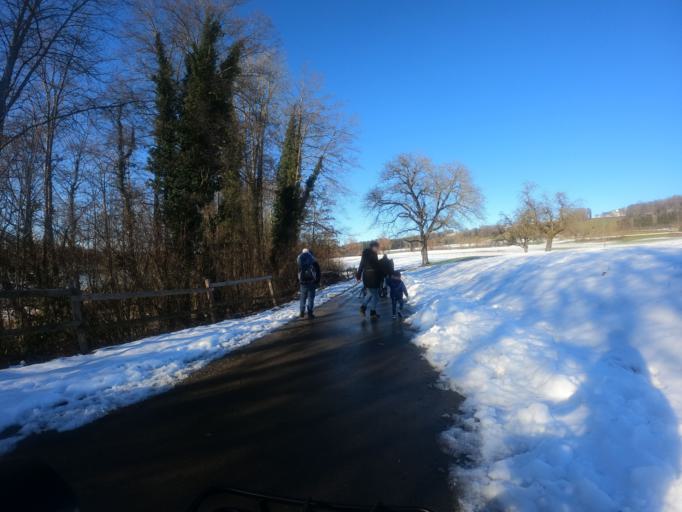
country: CH
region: Aargau
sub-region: Bezirk Bremgarten
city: Unterlunkhofen
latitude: 47.3247
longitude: 8.3748
